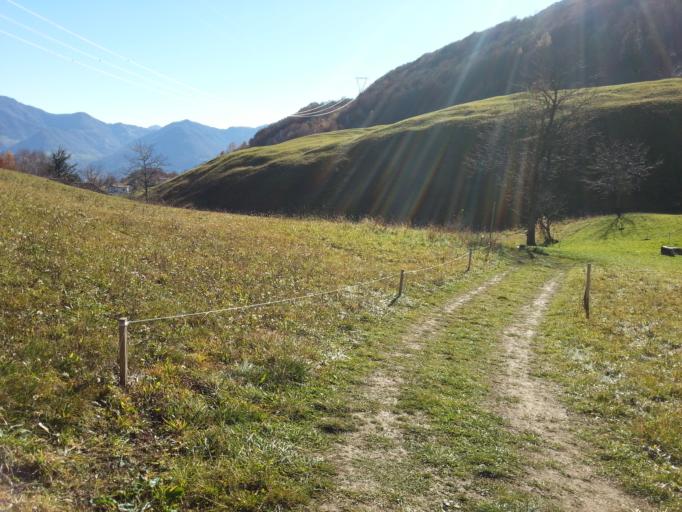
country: IT
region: Lombardy
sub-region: Provincia di Lecco
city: Primaluna
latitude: 45.9680
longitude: 9.4275
